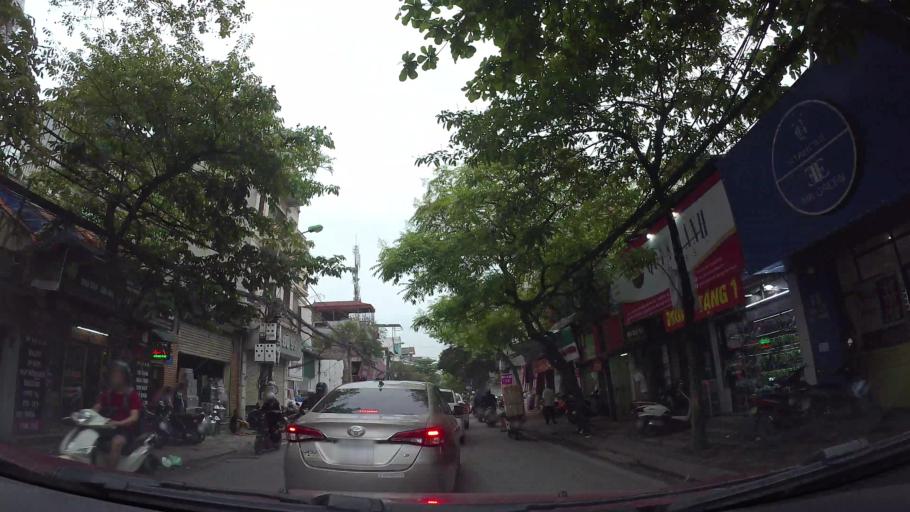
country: VN
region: Ha Noi
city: Hai BaTrung
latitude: 20.9961
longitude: 105.8477
